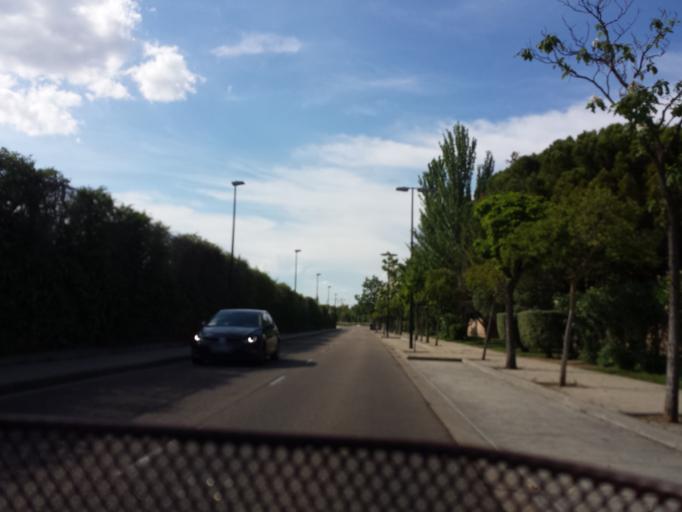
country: ES
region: Aragon
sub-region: Provincia de Zaragoza
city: Oliver-Valdefierro, Oliver, Valdefierro
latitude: 41.6324
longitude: -0.9210
